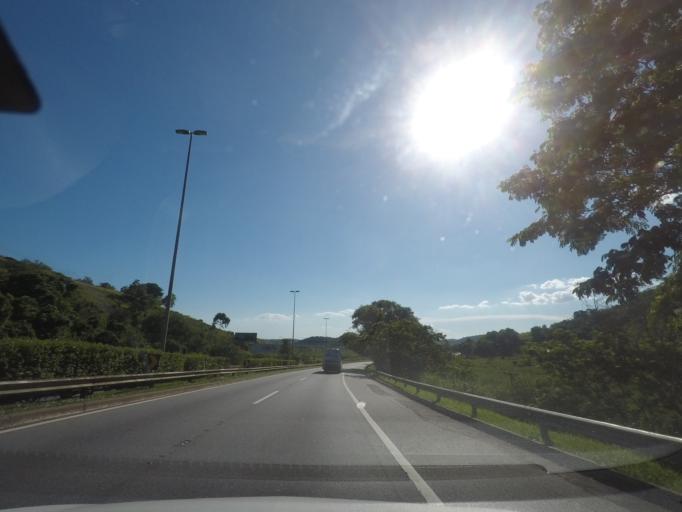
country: BR
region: Rio de Janeiro
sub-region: Sao Goncalo
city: Sao Goncalo
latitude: -22.6644
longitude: -43.0960
